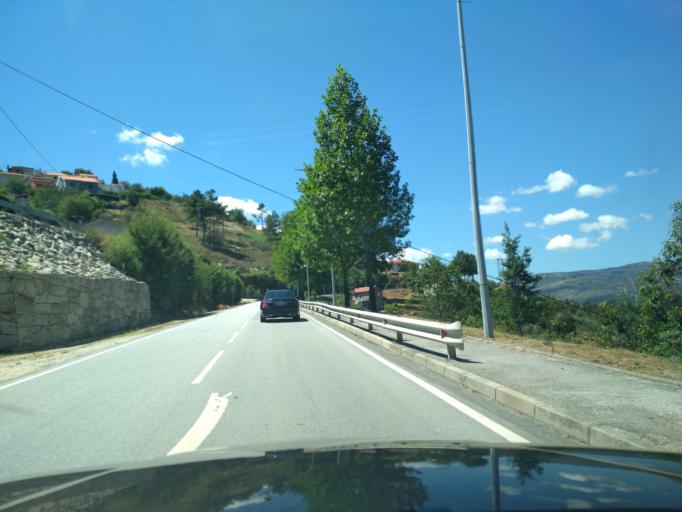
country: PT
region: Vila Real
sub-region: Ribeira de Pena
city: Ribeira de Pena
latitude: 41.5173
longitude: -7.7976
